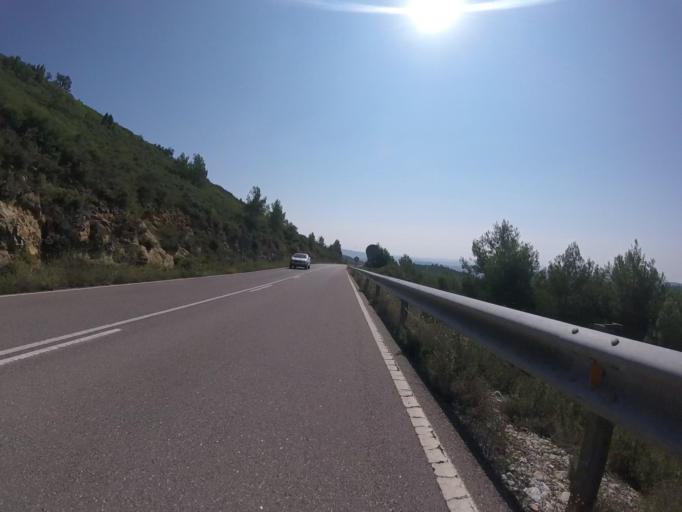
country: ES
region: Valencia
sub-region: Provincia de Castello
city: Benafigos
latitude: 40.2642
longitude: -0.2260
